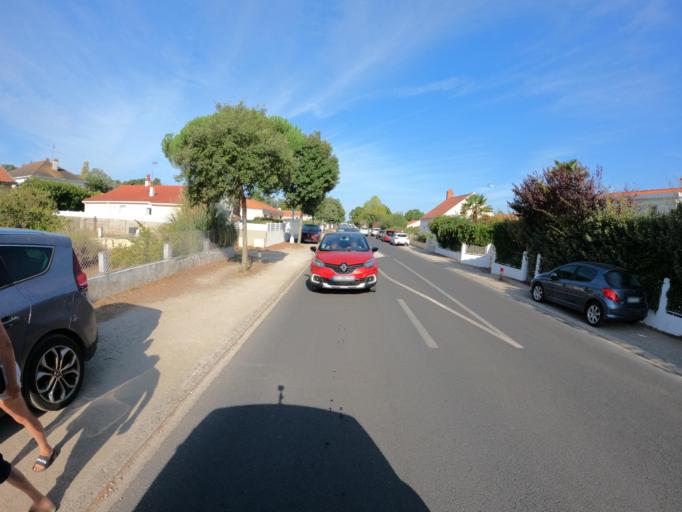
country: FR
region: Pays de la Loire
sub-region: Departement de la Vendee
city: Saint-Jean-de-Monts
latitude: 46.7992
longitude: -2.0746
